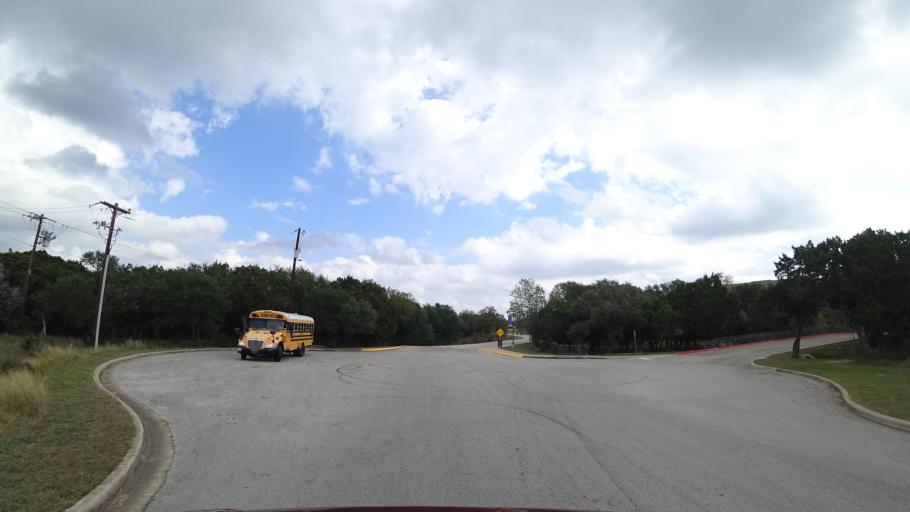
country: US
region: Texas
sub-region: Williamson County
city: Anderson Mill
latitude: 30.4208
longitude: -97.8419
